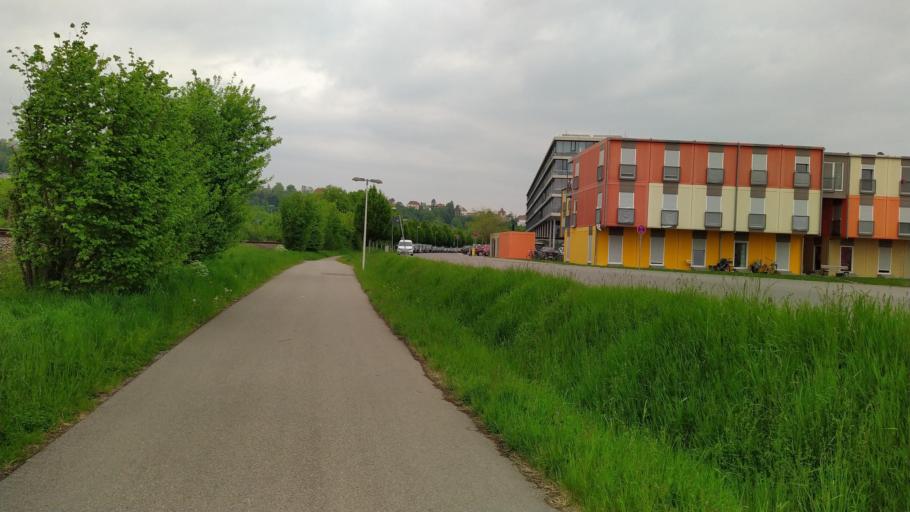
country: DE
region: Baden-Wuerttemberg
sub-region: Tuebingen Region
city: Tuebingen
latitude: 48.5092
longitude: 9.0465
